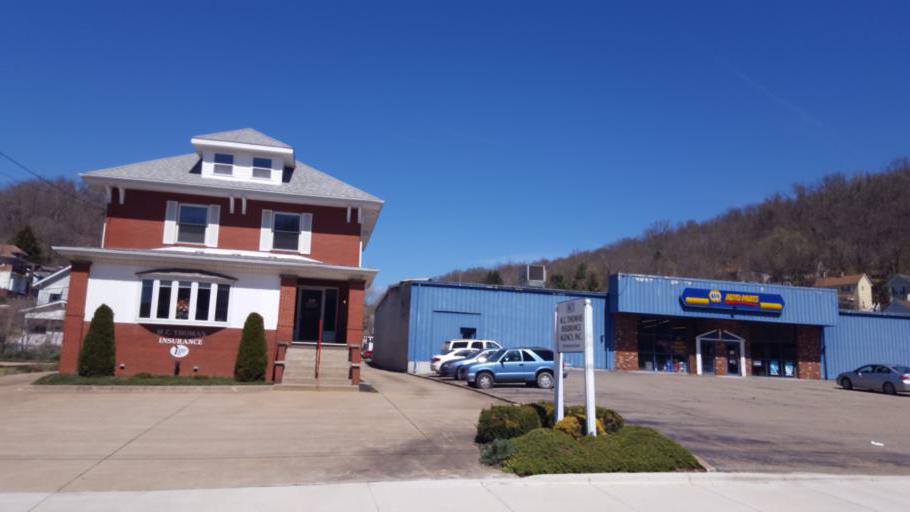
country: US
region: Ohio
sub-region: Belmont County
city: Bridgeport
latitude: 40.0705
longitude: -80.7597
